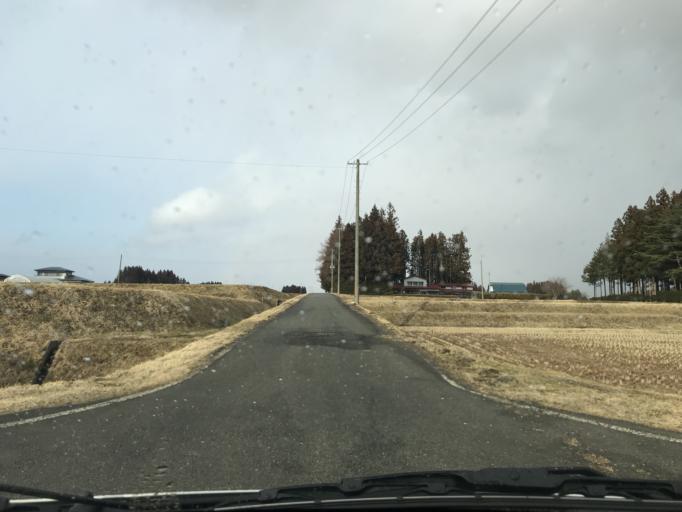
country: JP
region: Iwate
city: Mizusawa
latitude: 39.0888
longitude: 141.0281
